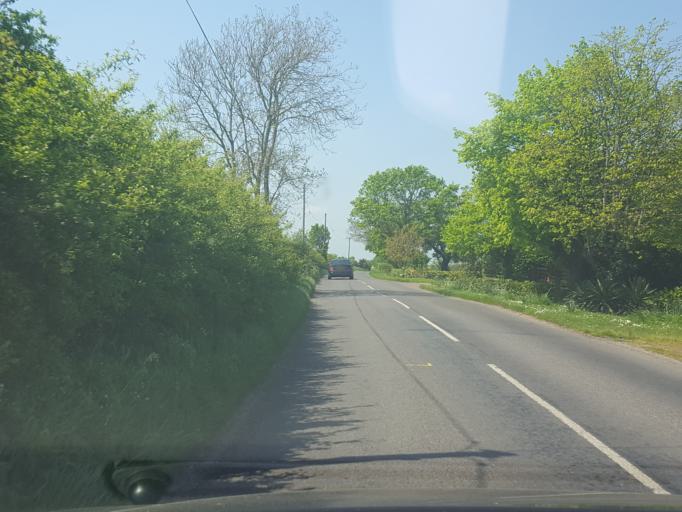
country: GB
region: England
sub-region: Essex
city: Great Bentley
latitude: 51.8545
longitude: 1.0829
